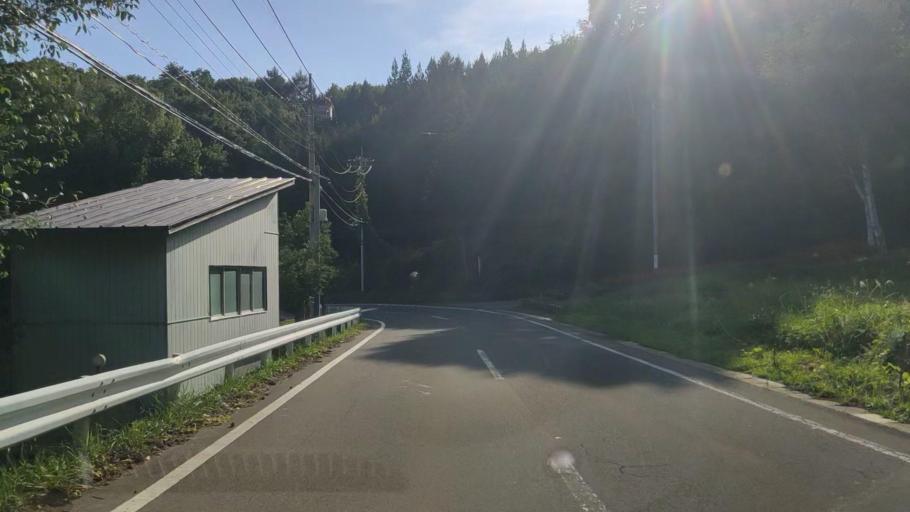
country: JP
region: Nagano
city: Suzaka
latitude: 36.5469
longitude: 138.5537
